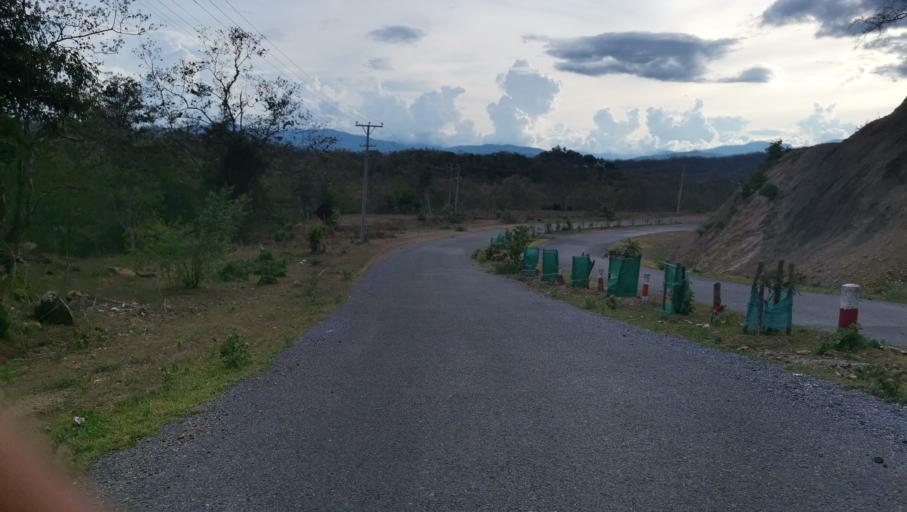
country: MM
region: Magway
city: Minbu
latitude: 20.1053
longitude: 94.5461
